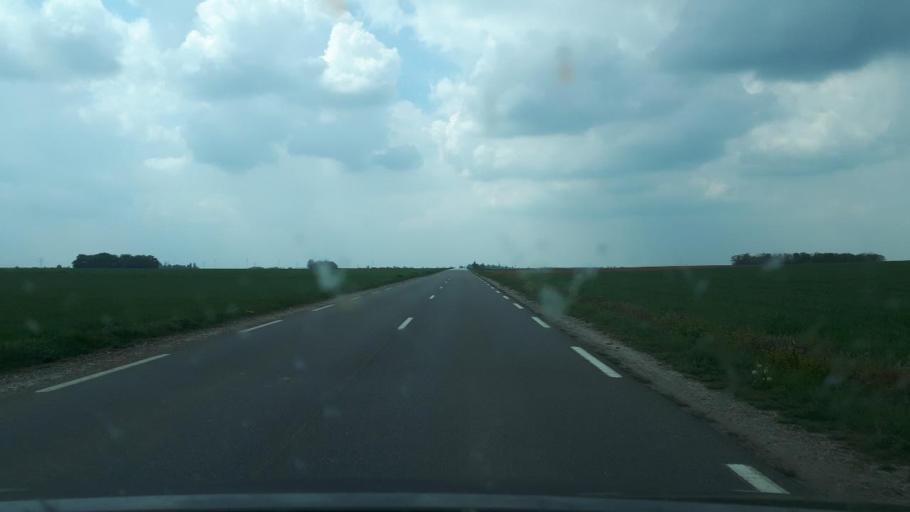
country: FR
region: Centre
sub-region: Departement du Loiret
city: Bazoches-les-Gallerandes
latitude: 48.1622
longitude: 2.0927
